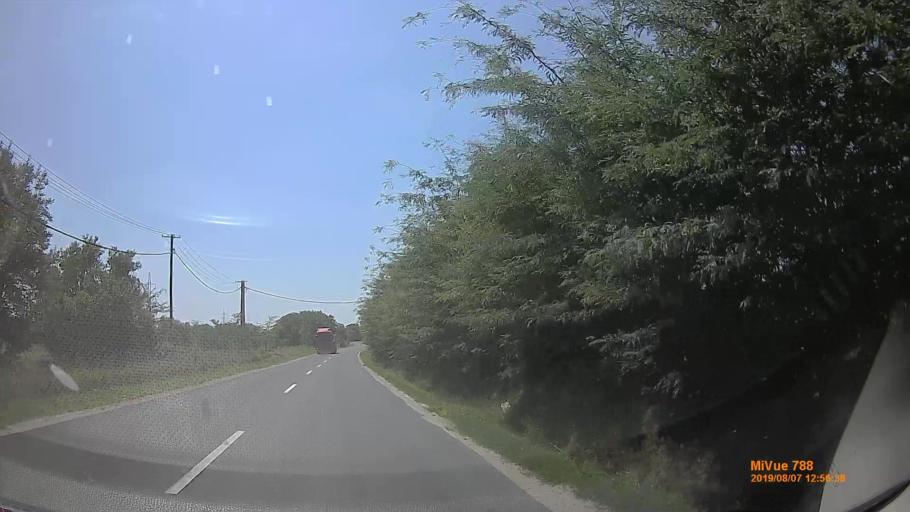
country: HU
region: Zala
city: Gyenesdias
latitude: 46.7953
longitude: 17.2659
